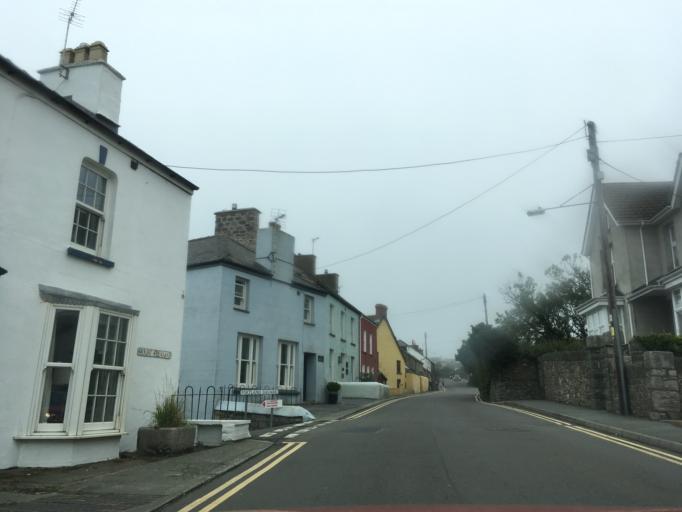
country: GB
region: Wales
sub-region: Pembrokeshire
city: Llanrhian
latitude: 51.8737
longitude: -5.1956
